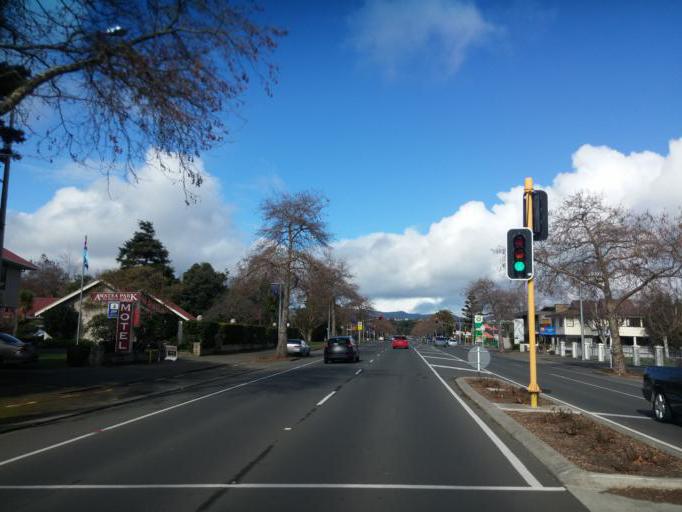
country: NZ
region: Manawatu-Wanganui
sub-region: Palmerston North City
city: Palmerston North
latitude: -40.3670
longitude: 175.6196
